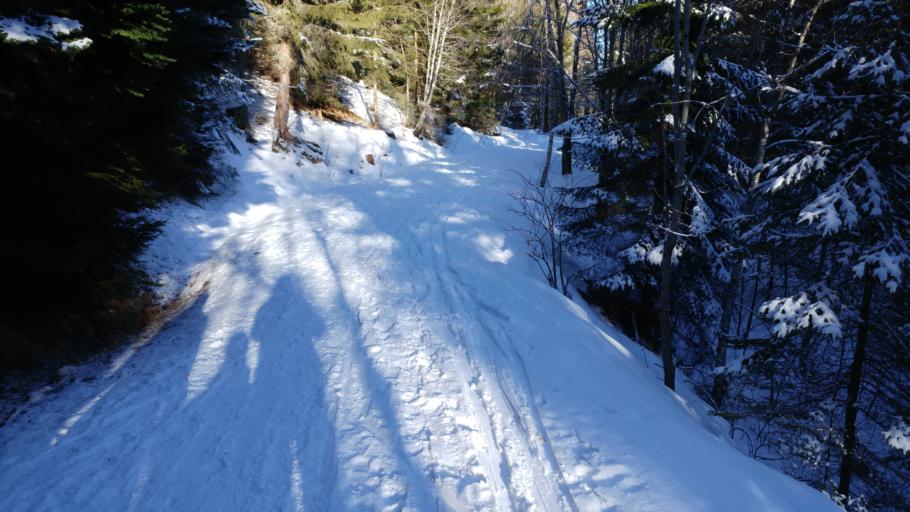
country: NO
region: Sor-Trondelag
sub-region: Trondheim
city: Trondheim
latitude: 63.4300
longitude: 10.3409
